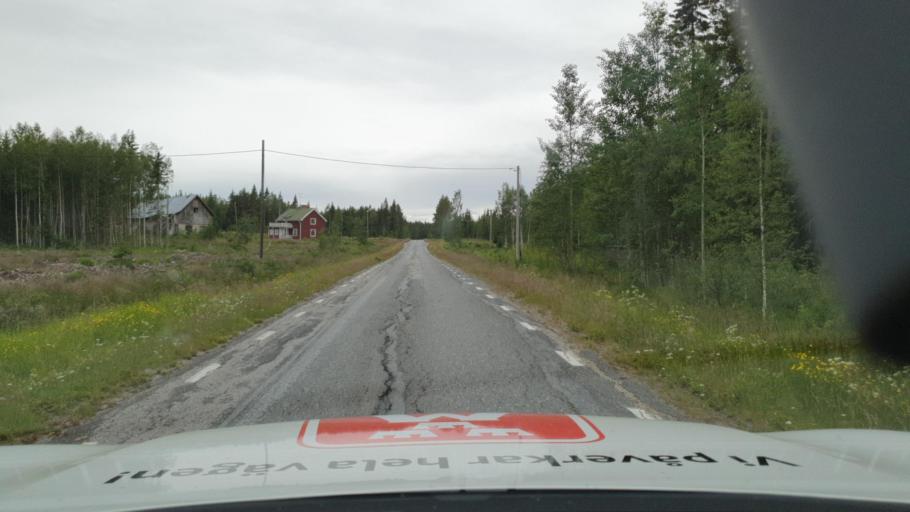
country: SE
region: Vaesterbotten
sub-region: Nordmalings Kommun
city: Nordmaling
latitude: 63.4828
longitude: 19.4503
